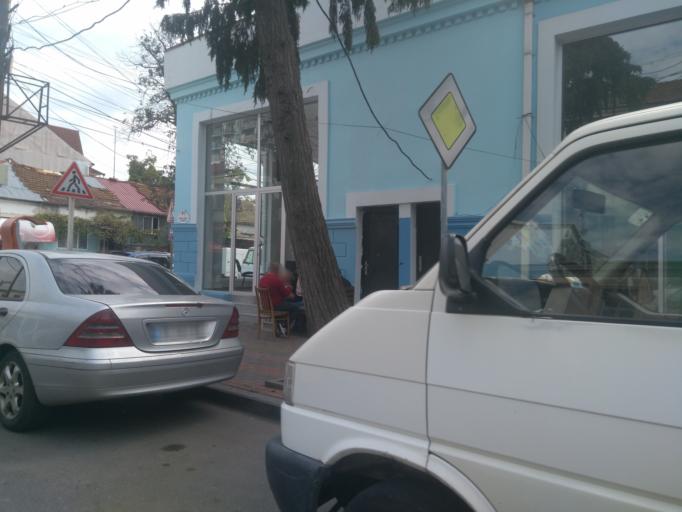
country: GE
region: Ajaria
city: Batumi
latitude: 41.6431
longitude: 41.6380
